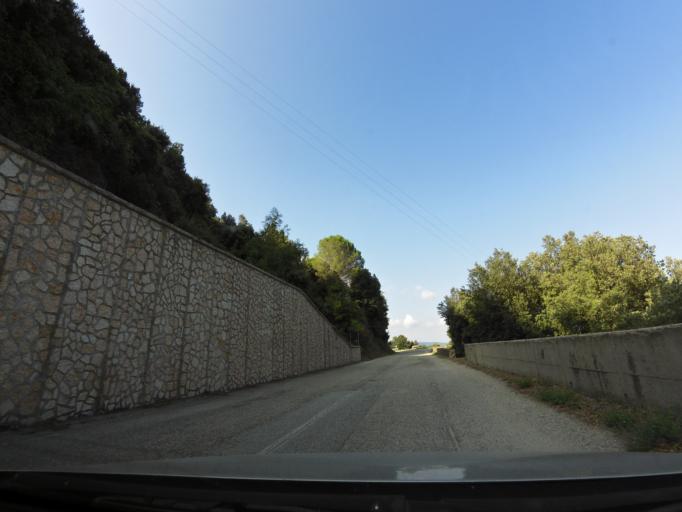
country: IT
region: Calabria
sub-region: Provincia di Reggio Calabria
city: Pazzano
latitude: 38.4666
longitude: 16.4242
